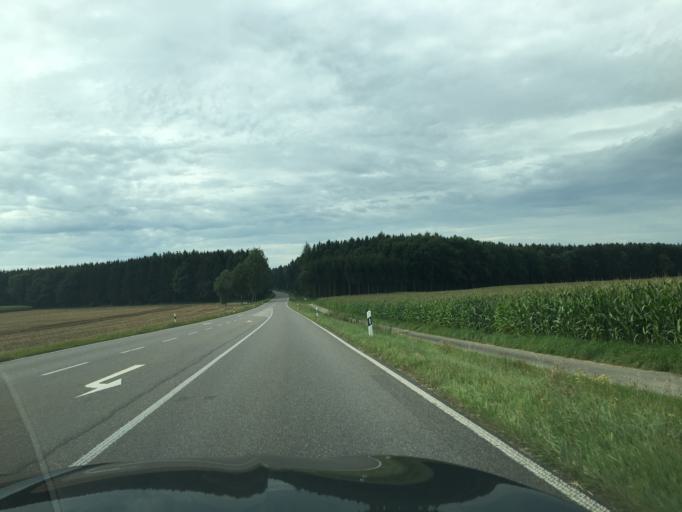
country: DE
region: Baden-Wuerttemberg
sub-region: Tuebingen Region
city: Emeringen
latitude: 48.2046
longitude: 9.5321
